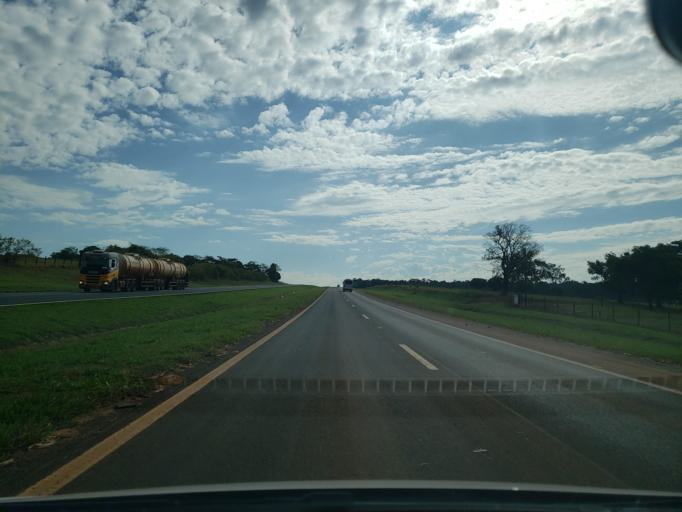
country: BR
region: Sao Paulo
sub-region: Promissao
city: Promissao
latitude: -21.6094
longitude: -49.8718
